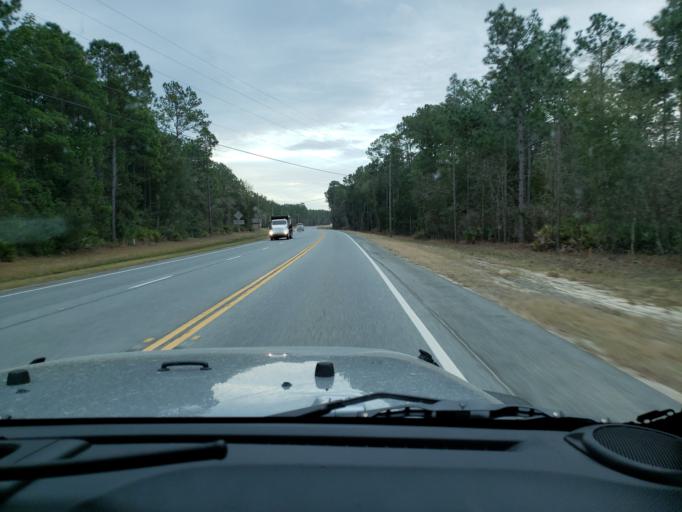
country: US
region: Georgia
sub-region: Chatham County
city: Bloomingdale
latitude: 32.0462
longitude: -81.3361
